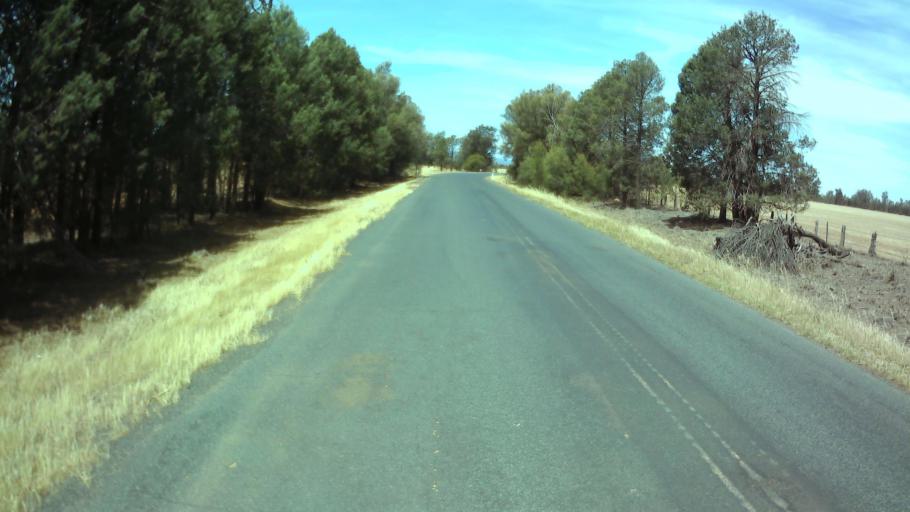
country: AU
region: New South Wales
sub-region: Weddin
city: Grenfell
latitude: -33.9417
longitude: 147.7735
